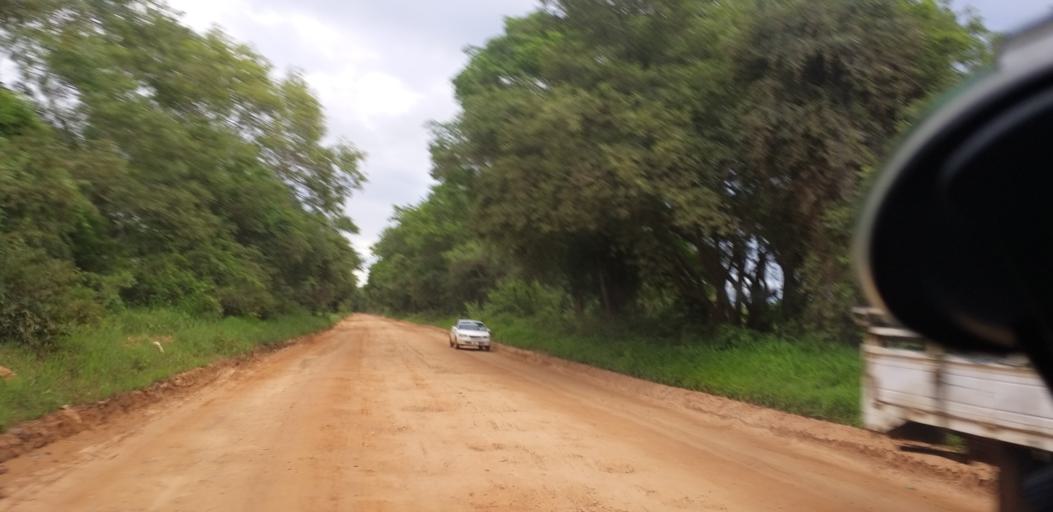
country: ZM
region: Lusaka
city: Lusaka
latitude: -15.1849
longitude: 28.4478
